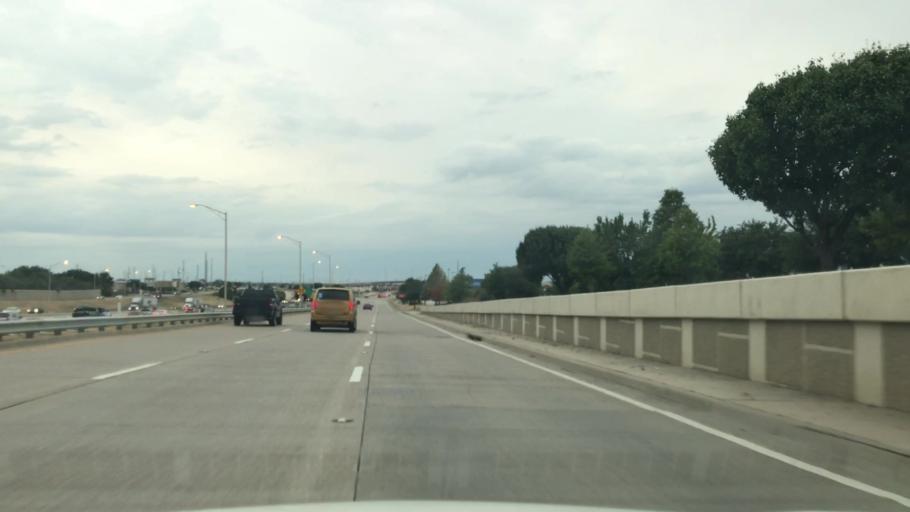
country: US
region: Texas
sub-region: Dallas County
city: Carrollton
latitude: 32.9844
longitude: -96.9026
